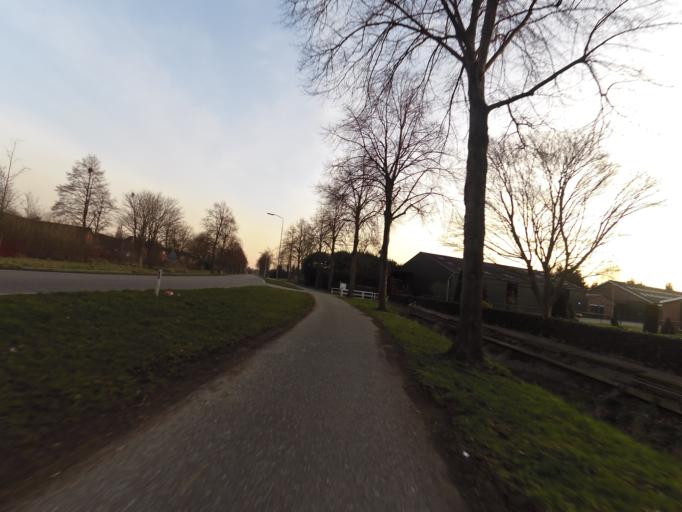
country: NL
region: Gelderland
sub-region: Gemeente Zevenaar
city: Zevenaar
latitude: 51.9369
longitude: 6.1207
